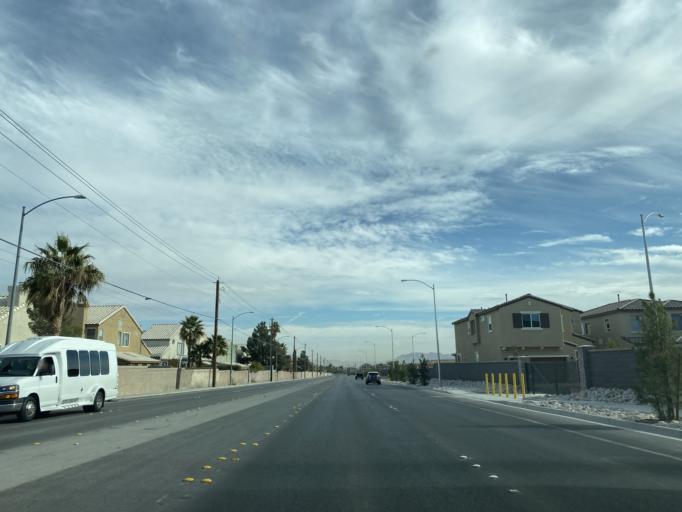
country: US
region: Nevada
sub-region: Clark County
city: North Las Vegas
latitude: 36.2467
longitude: -115.1644
